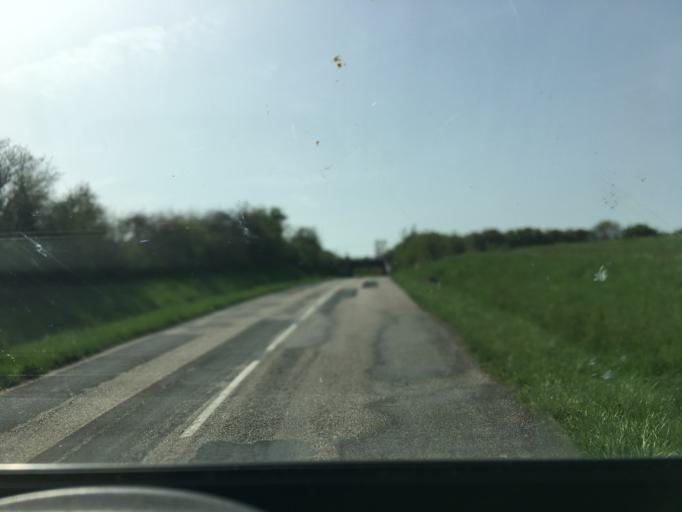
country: FR
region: Lorraine
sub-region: Departement de Meurthe-et-Moselle
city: Fleville-devant-Nancy
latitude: 48.6199
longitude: 6.2282
